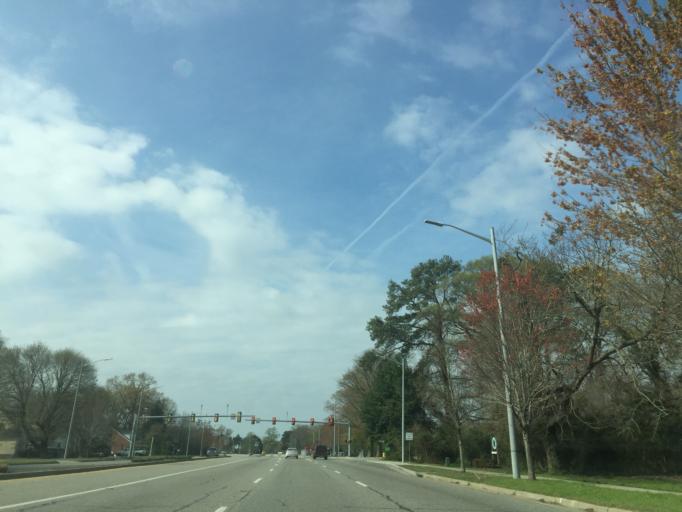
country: US
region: Virginia
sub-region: City of Newport News
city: Newport News
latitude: 37.0616
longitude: -76.4627
